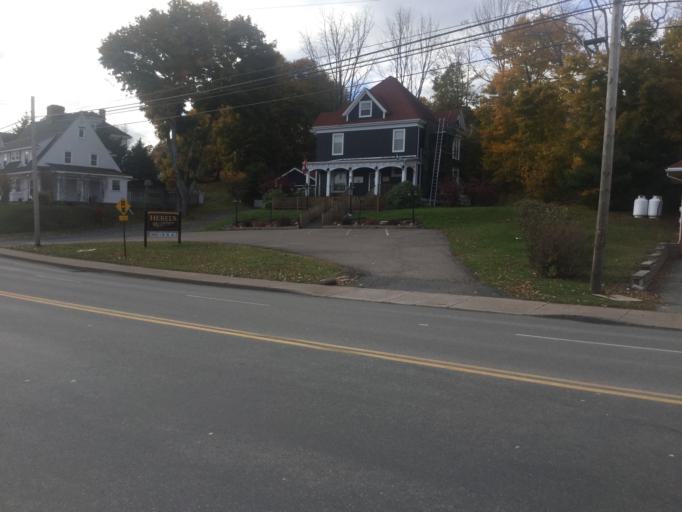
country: CA
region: Nova Scotia
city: New Glasgow
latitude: 45.5891
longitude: -62.6502
